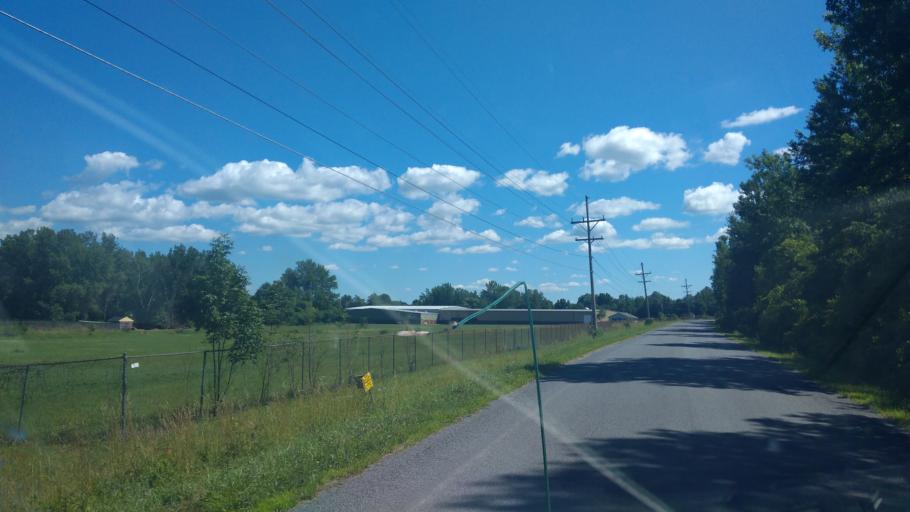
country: US
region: New York
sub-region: Wayne County
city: Sodus
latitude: 43.2098
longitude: -77.0243
